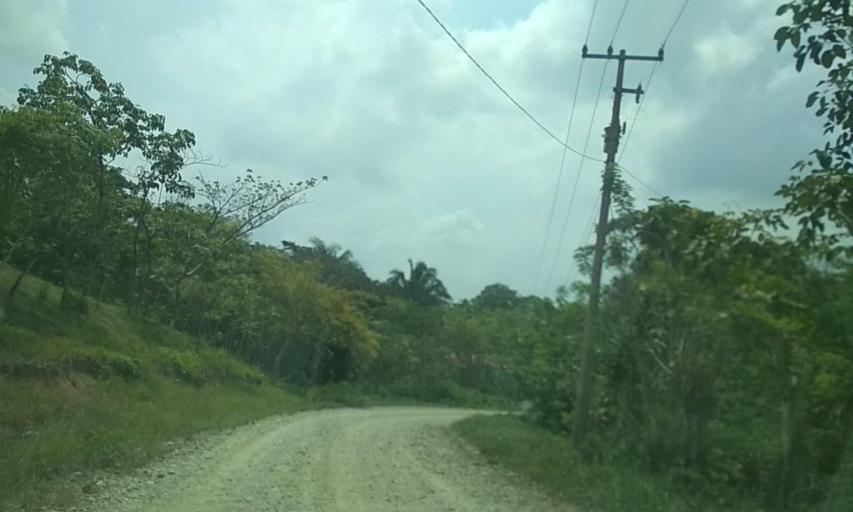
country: MX
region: Tabasco
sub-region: Huimanguillo
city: Francisco Rueda
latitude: 17.6277
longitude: -93.8191
